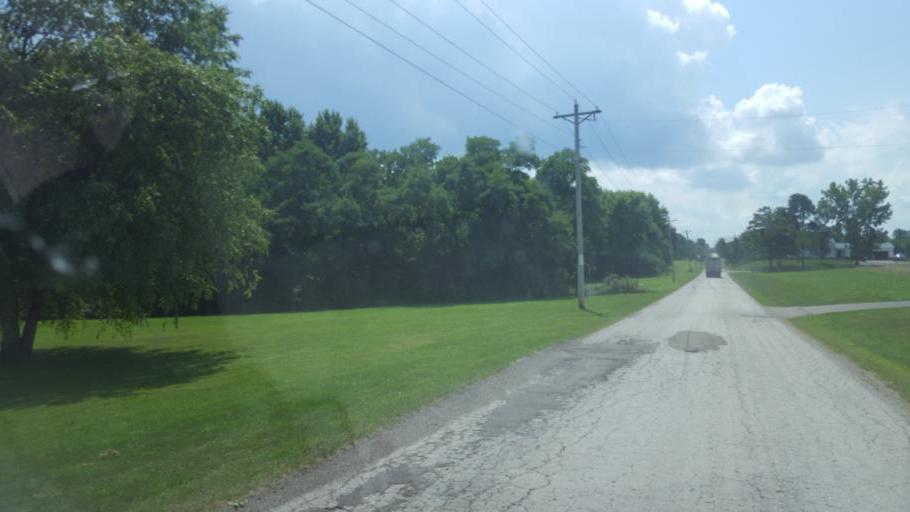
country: US
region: Ohio
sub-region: Knox County
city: Centerburg
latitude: 40.3949
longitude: -82.6525
